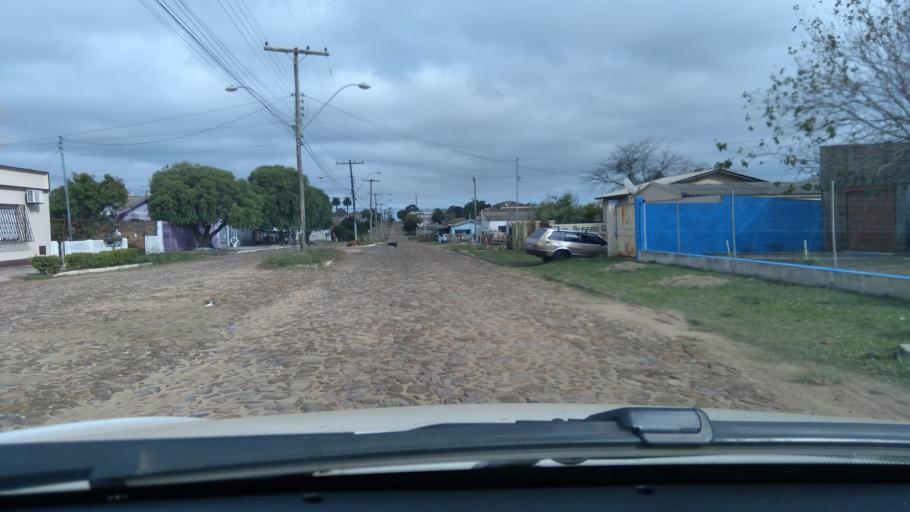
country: BR
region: Rio Grande do Sul
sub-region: Dom Pedrito
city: Dom Pedrito
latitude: -30.9824
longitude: -54.6625
